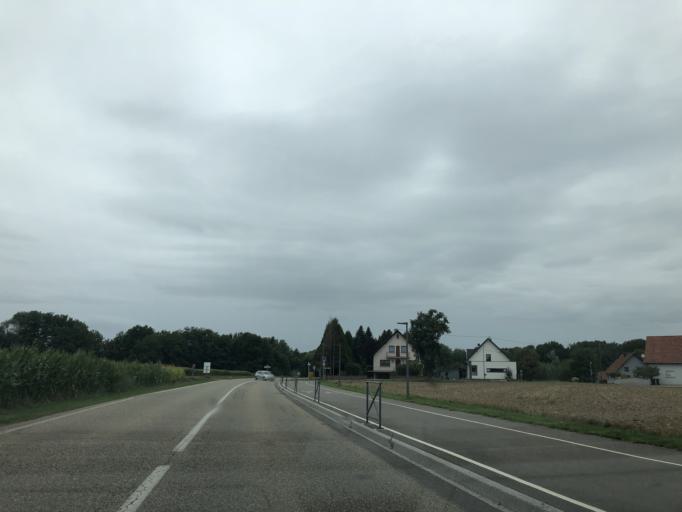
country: DE
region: Rheinland-Pfalz
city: Scheibenhardt
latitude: 48.9778
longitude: 8.1326
